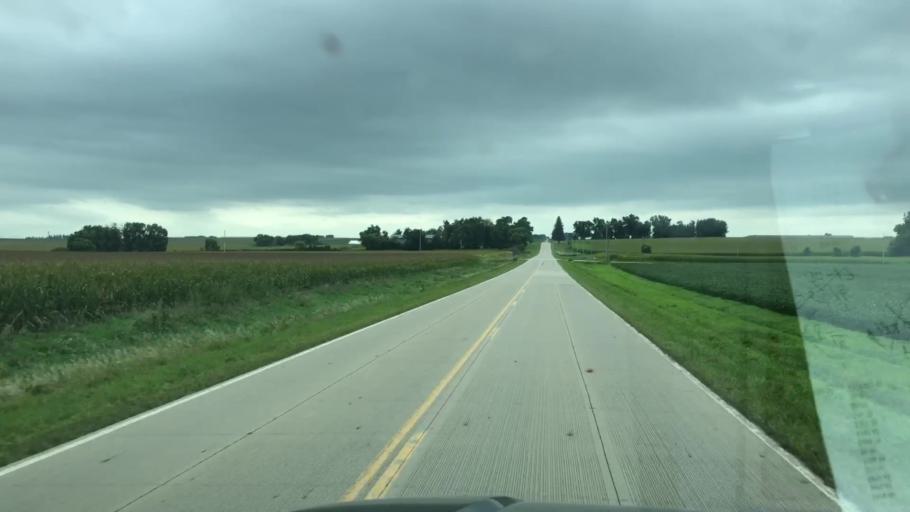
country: US
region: Iowa
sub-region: Sioux County
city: Alton
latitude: 43.1151
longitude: -95.9788
